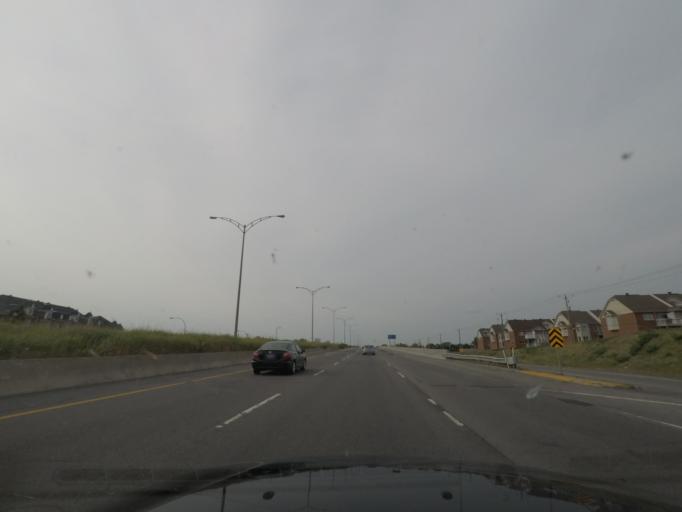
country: CA
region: Quebec
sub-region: Monteregie
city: La Prairie
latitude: 45.4325
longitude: -73.4906
